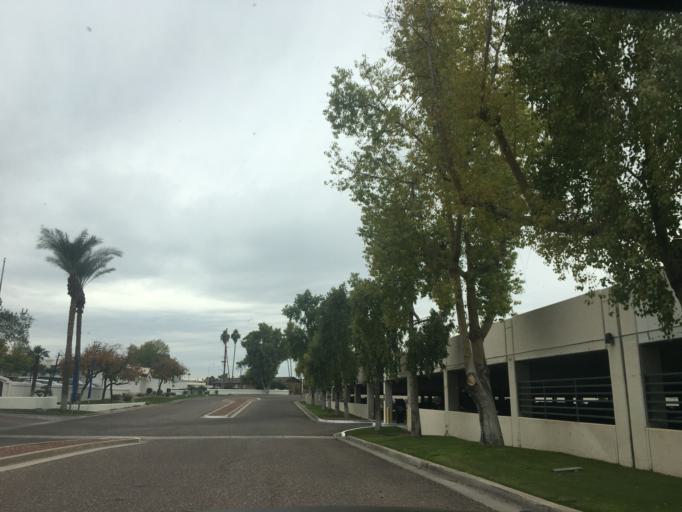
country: US
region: Arizona
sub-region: Maricopa County
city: Tempe Junction
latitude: 33.3810
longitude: -111.9259
